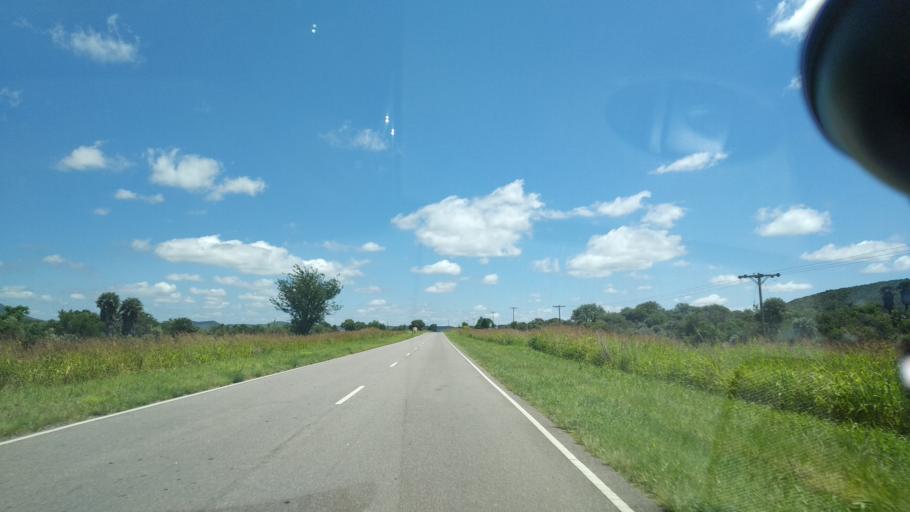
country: AR
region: Cordoba
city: Salsacate
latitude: -31.3974
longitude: -65.0976
